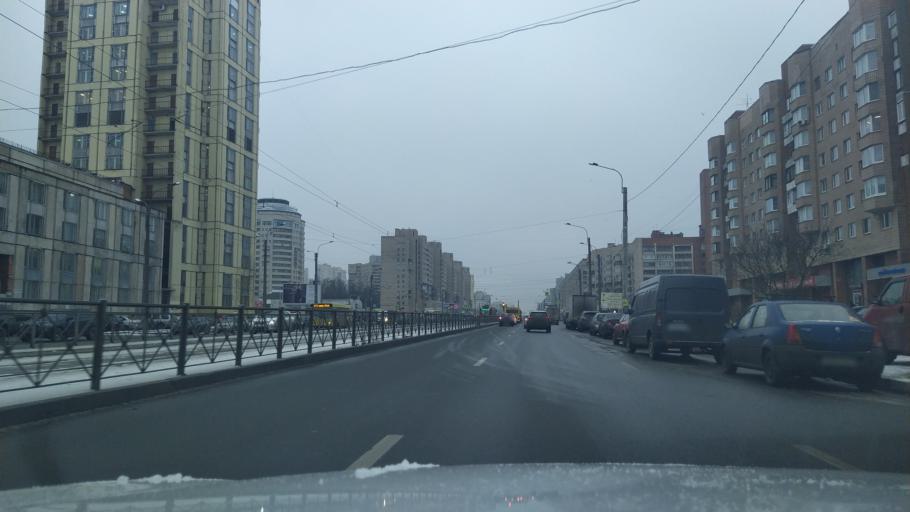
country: RU
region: St.-Petersburg
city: Grazhdanka
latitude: 60.0349
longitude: 30.4234
